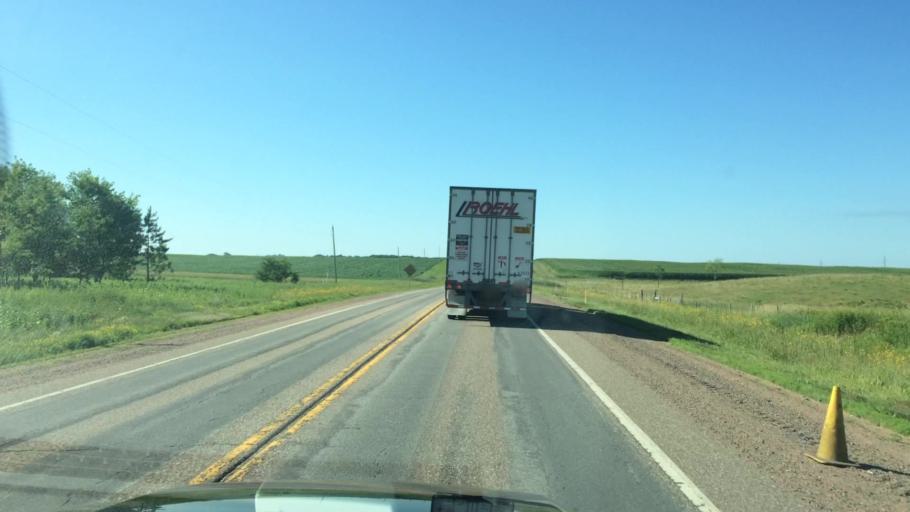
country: US
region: Wisconsin
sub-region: Marathon County
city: Athens
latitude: 44.9246
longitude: -90.0787
